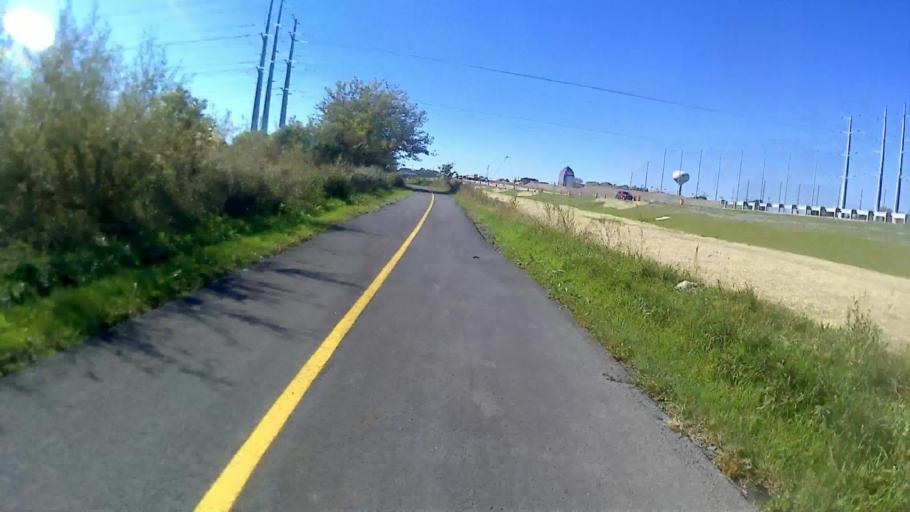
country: US
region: Illinois
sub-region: DuPage County
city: Itasca
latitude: 41.9828
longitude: -87.9920
